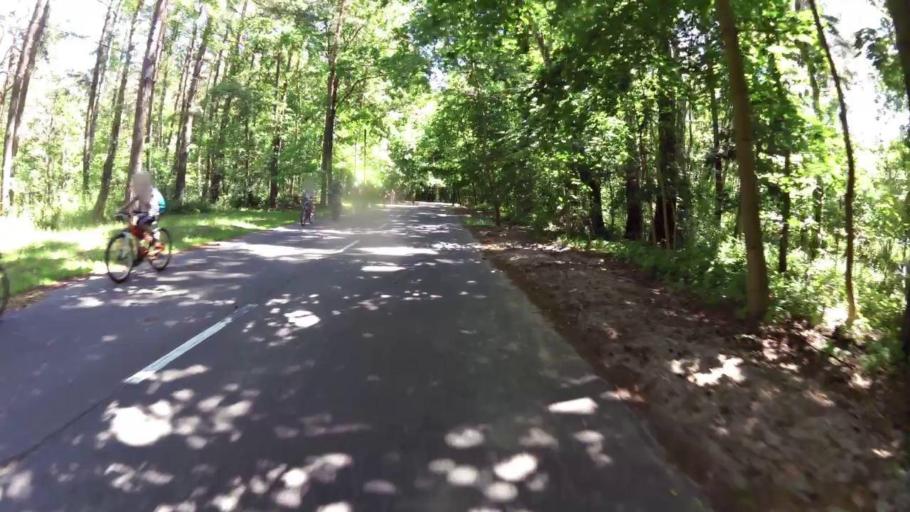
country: PL
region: West Pomeranian Voivodeship
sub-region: Powiat gryficki
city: Cerkwica
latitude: 54.0945
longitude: 15.1279
